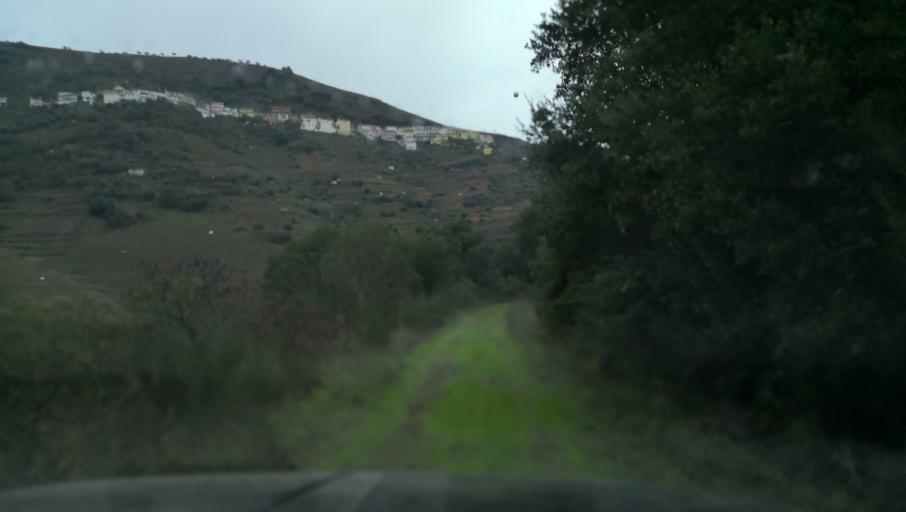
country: PT
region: Vila Real
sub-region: Peso da Regua
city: Peso da Regua
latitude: 41.1819
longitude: -7.7587
